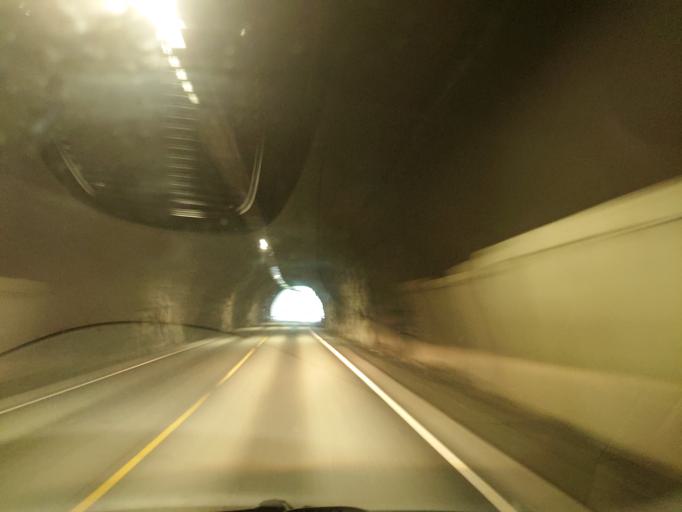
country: NO
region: Hordaland
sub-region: Osteroy
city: Lonevag
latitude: 60.6993
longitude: 5.5847
